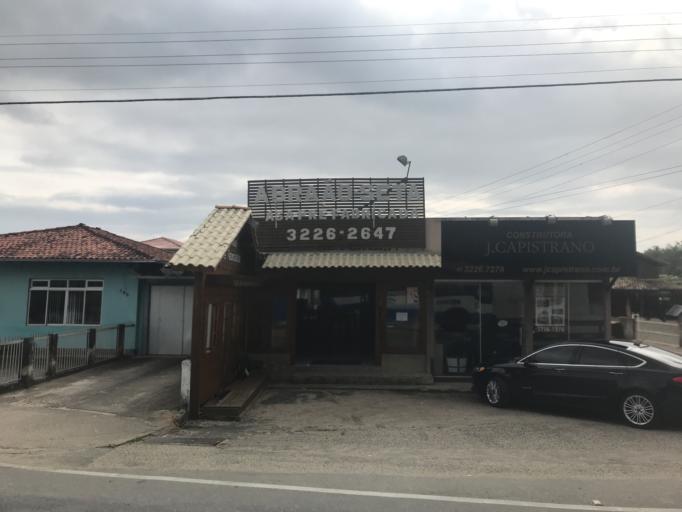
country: BR
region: Santa Catarina
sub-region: Florianopolis
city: Costeira do Pirajubae
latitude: -27.6480
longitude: -48.5216
